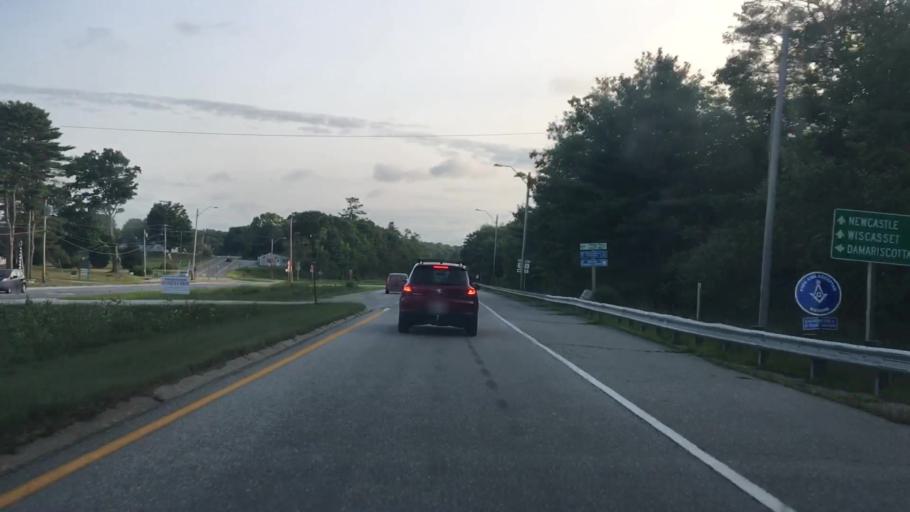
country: US
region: Maine
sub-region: Lincoln County
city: Nobleboro
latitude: 44.0559
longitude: -69.4997
